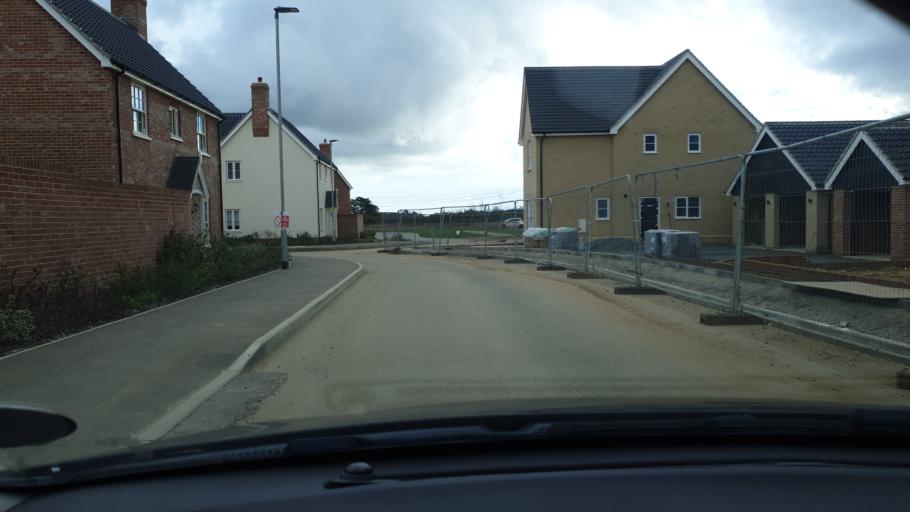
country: GB
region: England
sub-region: Essex
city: Mistley
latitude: 51.9394
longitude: 1.0932
